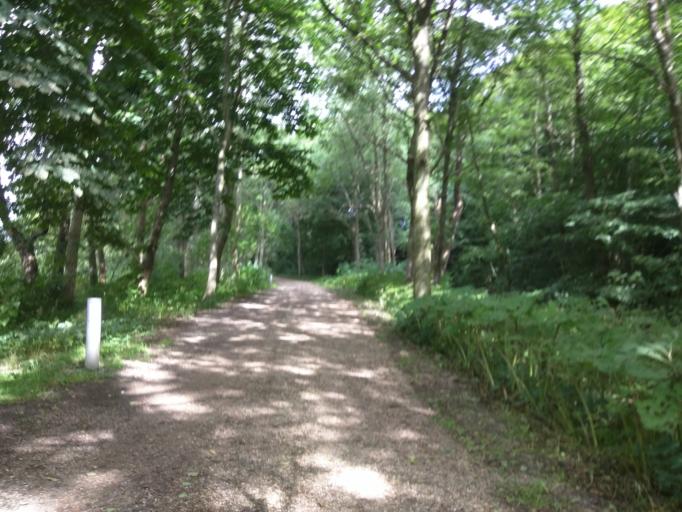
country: DK
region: Central Jutland
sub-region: Viborg Kommune
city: Viborg
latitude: 56.4465
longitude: 9.4224
